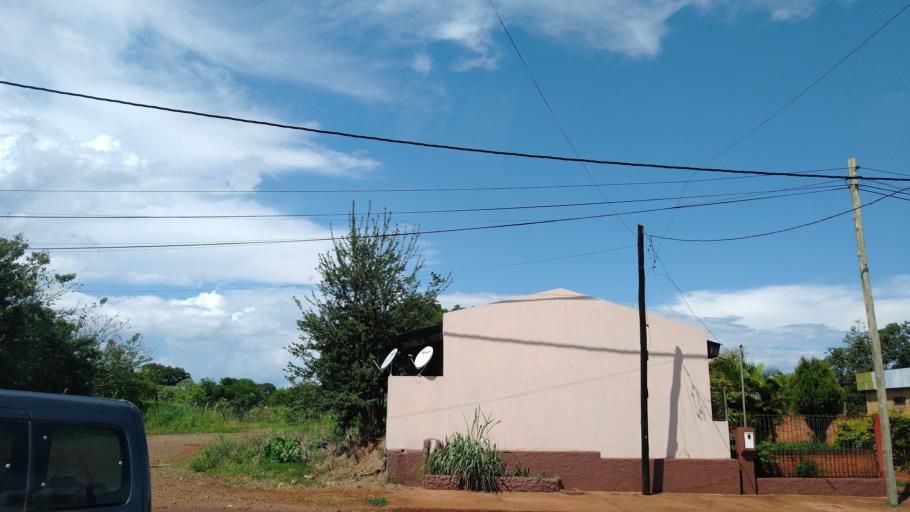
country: AR
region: Misiones
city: Puerto Libertad
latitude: -25.9690
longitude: -54.5718
